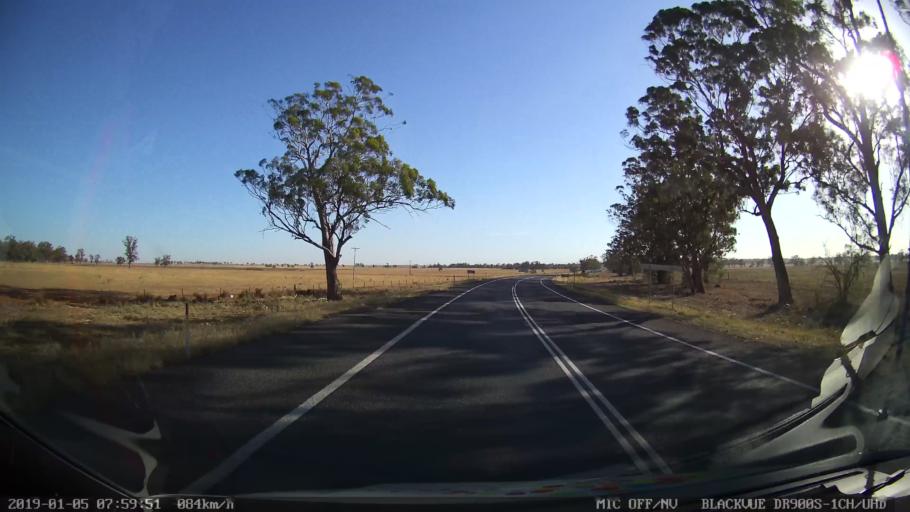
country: AU
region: New South Wales
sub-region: Gilgandra
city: Gilgandra
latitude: -31.6972
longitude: 148.6806
